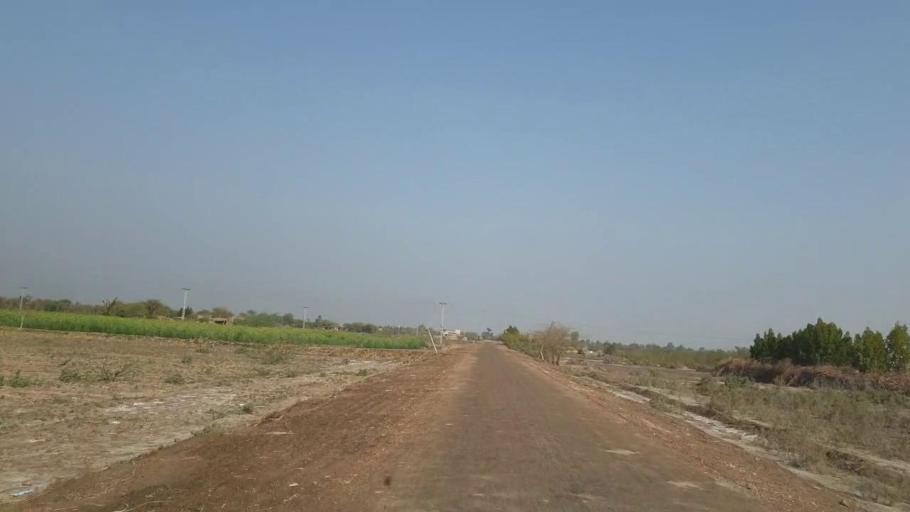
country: PK
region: Sindh
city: Mirpur Khas
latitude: 25.5930
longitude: 69.0148
